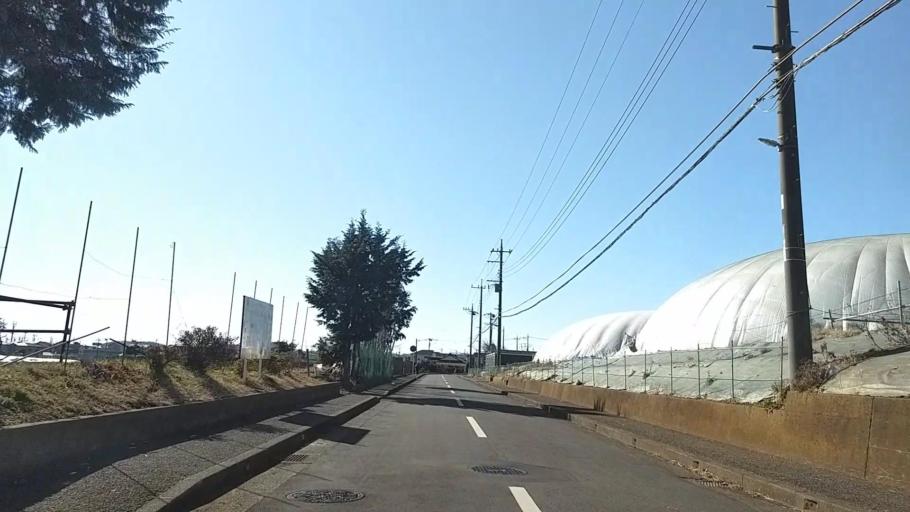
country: JP
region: Kanagawa
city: Hadano
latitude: 35.3955
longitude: 139.1916
